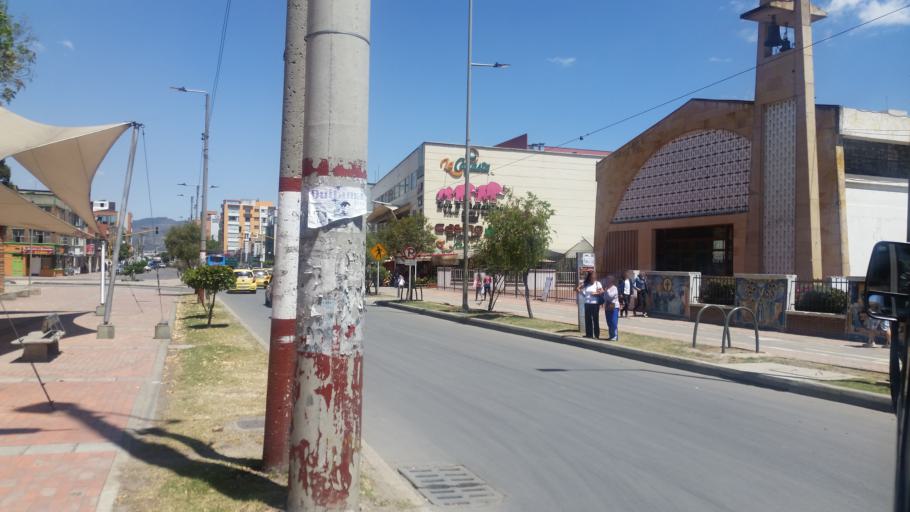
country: CO
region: Boyaca
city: Sogamoso
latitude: 5.7238
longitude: -72.9238
